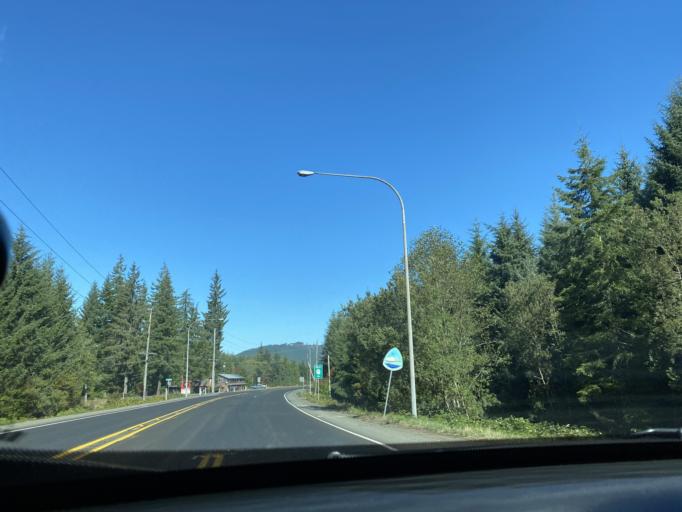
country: US
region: Washington
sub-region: Clallam County
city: Forks
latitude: 47.9663
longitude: -124.4030
